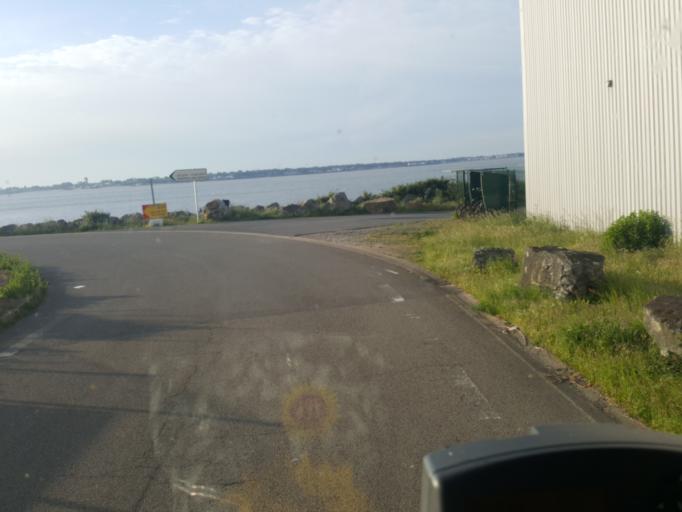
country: FR
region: Pays de la Loire
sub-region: Departement de la Loire-Atlantique
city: Saint-Nazaire
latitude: 47.2792
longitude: -2.1912
